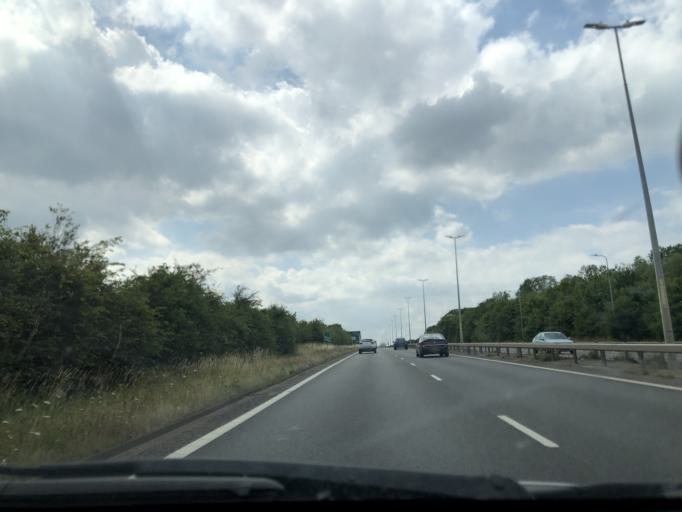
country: GB
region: England
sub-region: Kent
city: Whitstable
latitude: 51.3394
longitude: 1.0329
